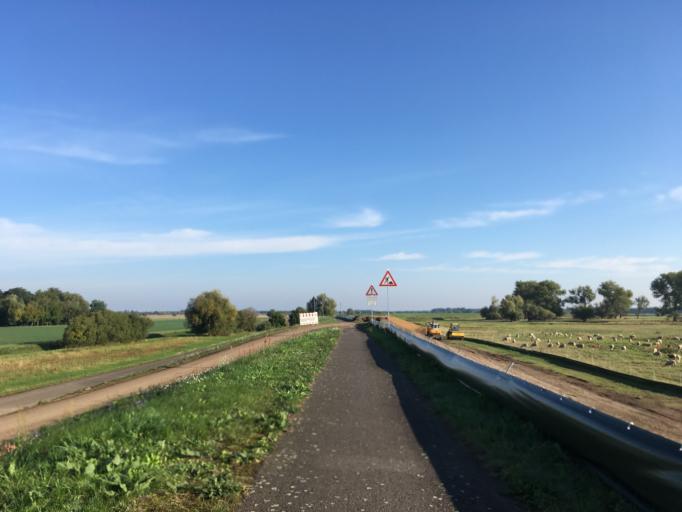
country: DE
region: Brandenburg
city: Reitwein
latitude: 52.4572
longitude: 14.5911
